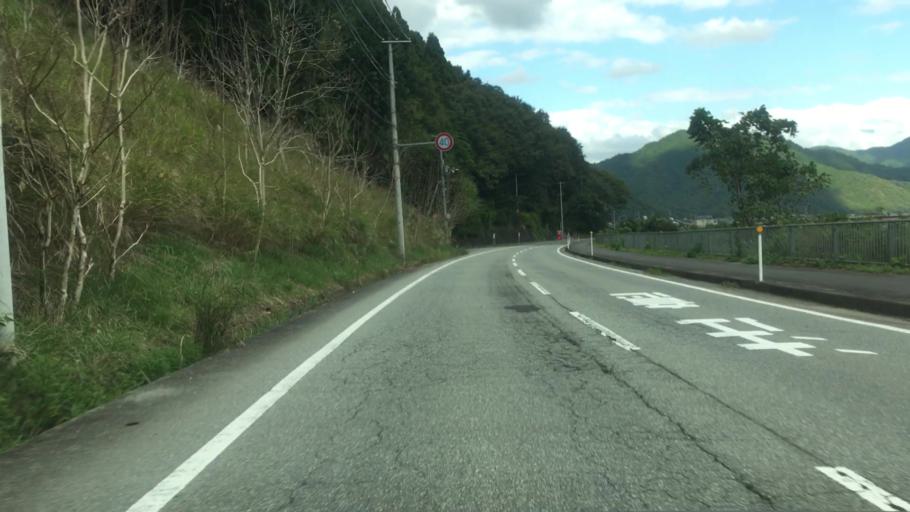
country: JP
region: Hyogo
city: Toyooka
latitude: 35.3681
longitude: 134.7615
